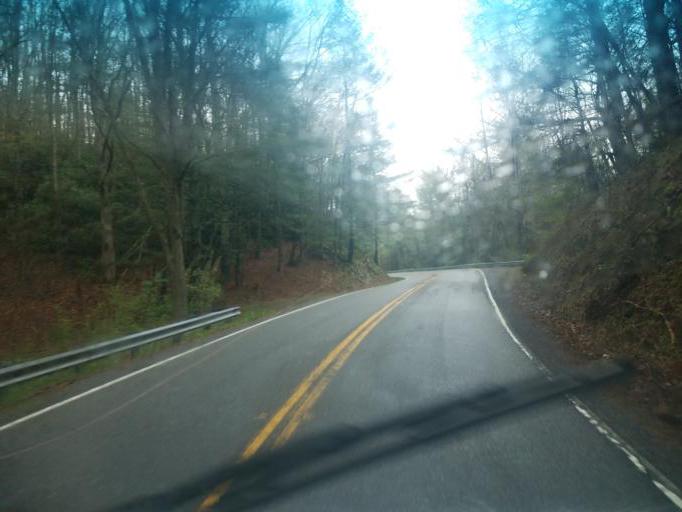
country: US
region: Virginia
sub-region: Smyth County
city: Chilhowie
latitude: 36.6545
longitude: -81.6886
